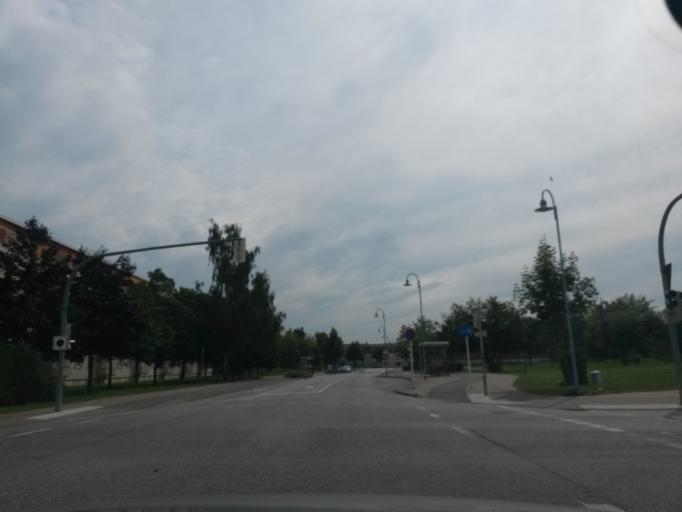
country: DE
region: Brandenburg
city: Schwedt (Oder)
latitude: 53.0544
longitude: 14.2782
